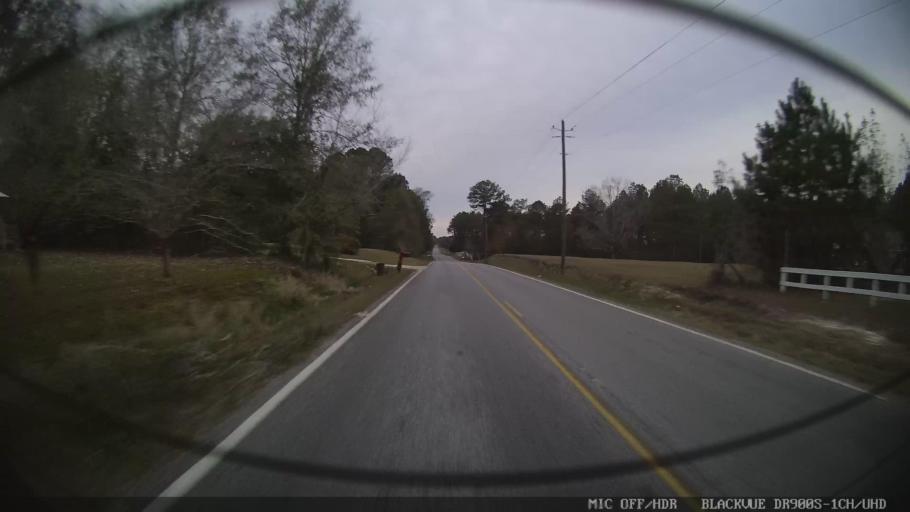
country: US
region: Mississippi
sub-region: Clarke County
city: Quitman
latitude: 32.0291
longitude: -88.7980
